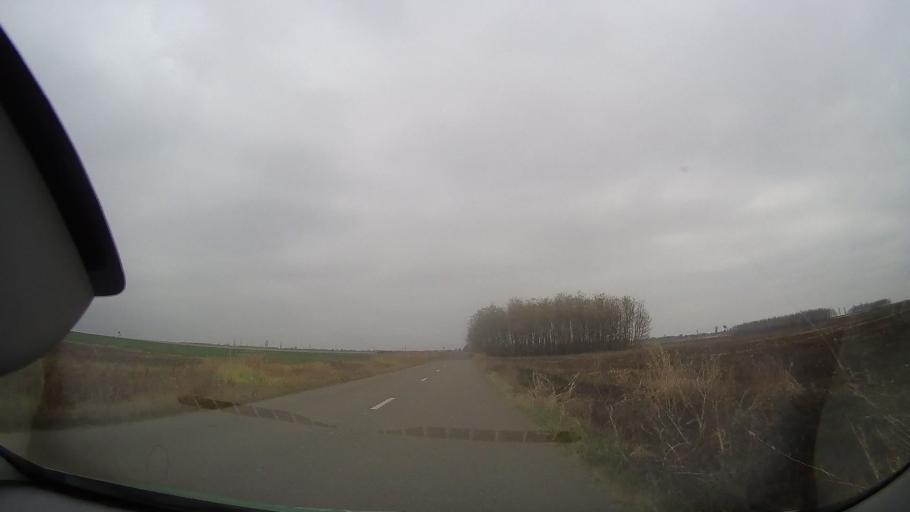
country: RO
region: Buzau
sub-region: Comuna Scutelnici
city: Scutelnici
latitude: 44.8631
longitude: 26.8975
